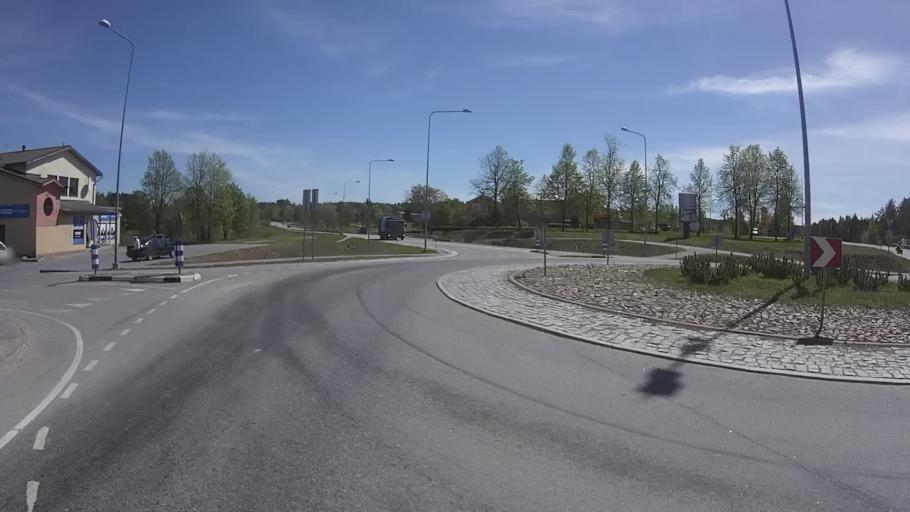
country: EE
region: Vorumaa
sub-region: Voru linn
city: Voru
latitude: 57.8159
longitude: 27.0295
